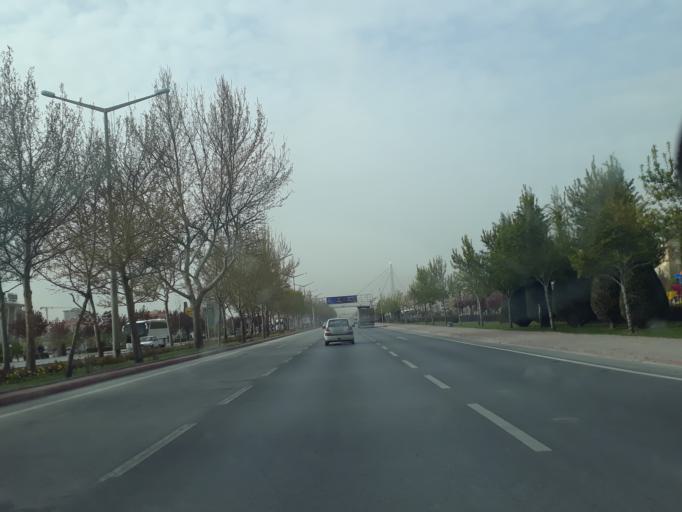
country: TR
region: Konya
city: Selcuklu
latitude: 37.9683
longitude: 32.5153
